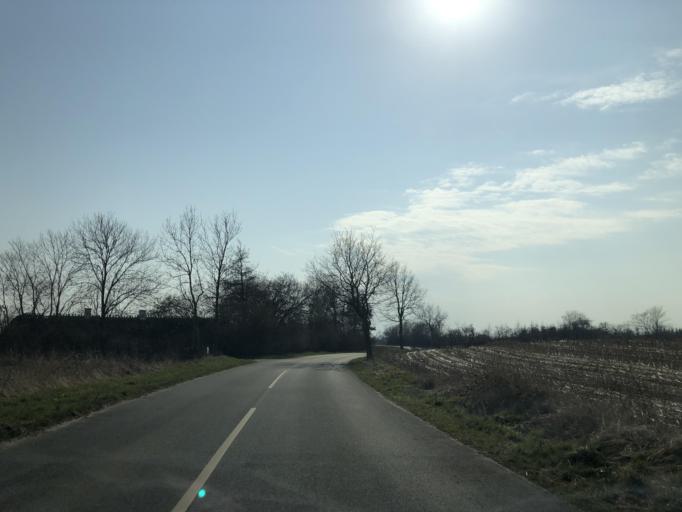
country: DK
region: South Denmark
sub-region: Sonderborg Kommune
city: Nordborg
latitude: 55.0736
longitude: 9.7312
